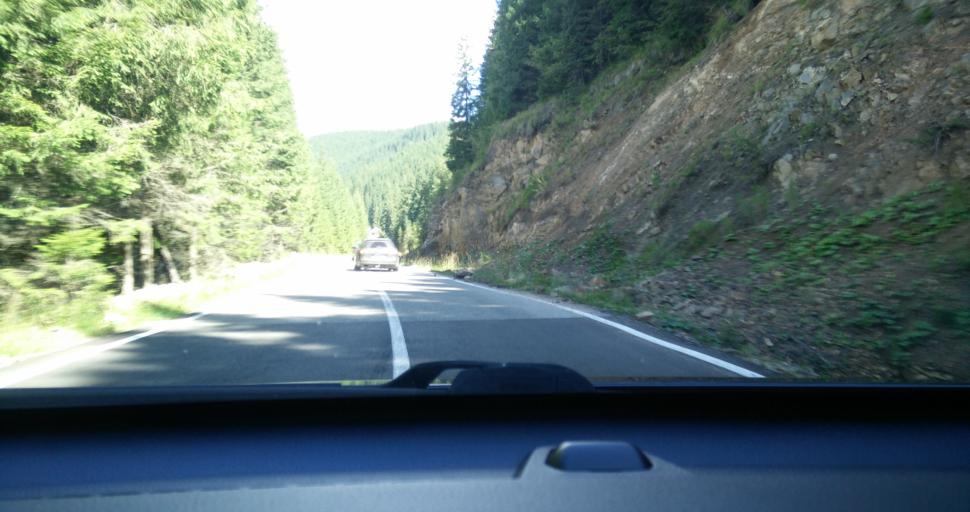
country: RO
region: Alba
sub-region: Comuna Sugag
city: Sugag
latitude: 45.5367
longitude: 23.6396
